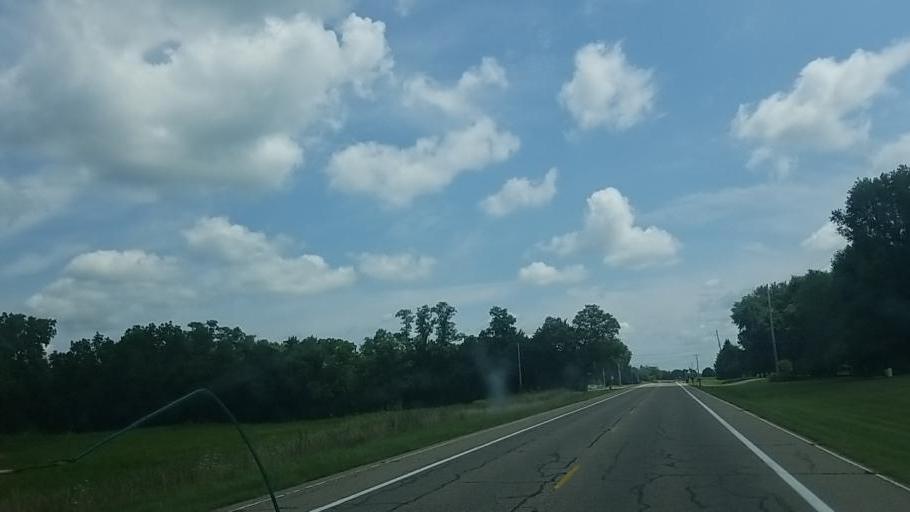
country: US
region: Ohio
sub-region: Fairfield County
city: Pickerington
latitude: 39.8778
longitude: -82.7274
